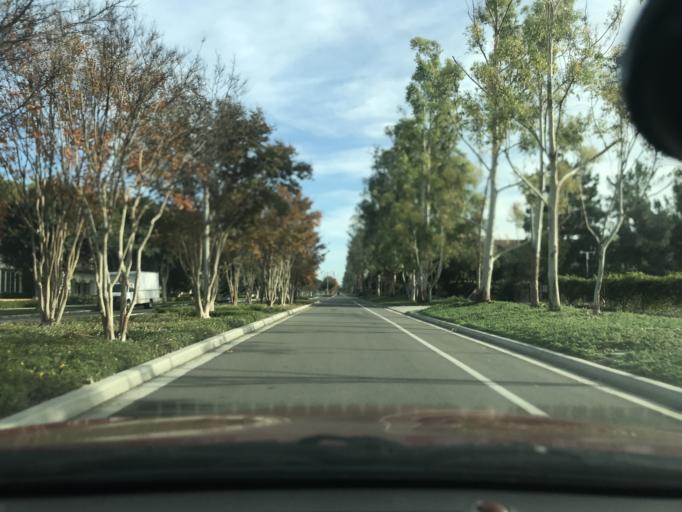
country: US
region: California
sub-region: Orange County
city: Irvine
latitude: 33.6969
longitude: -117.7559
